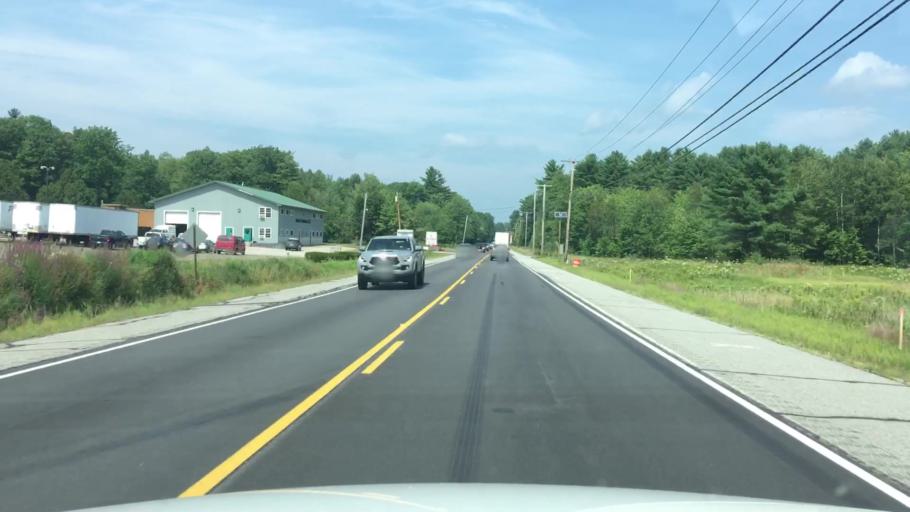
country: US
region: Maine
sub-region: Androscoggin County
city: Turner
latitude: 44.2328
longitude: -70.2552
